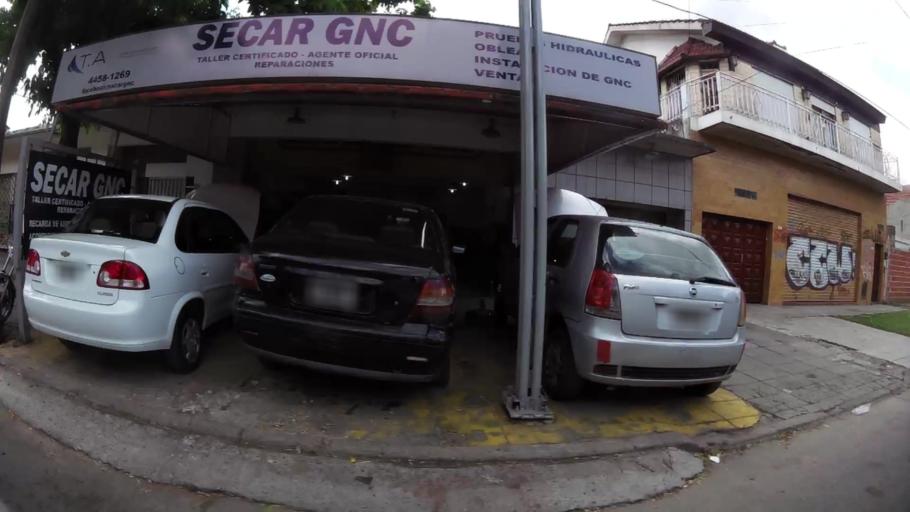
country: AR
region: Buenos Aires
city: Ituzaingo
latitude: -34.6390
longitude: -58.6630
